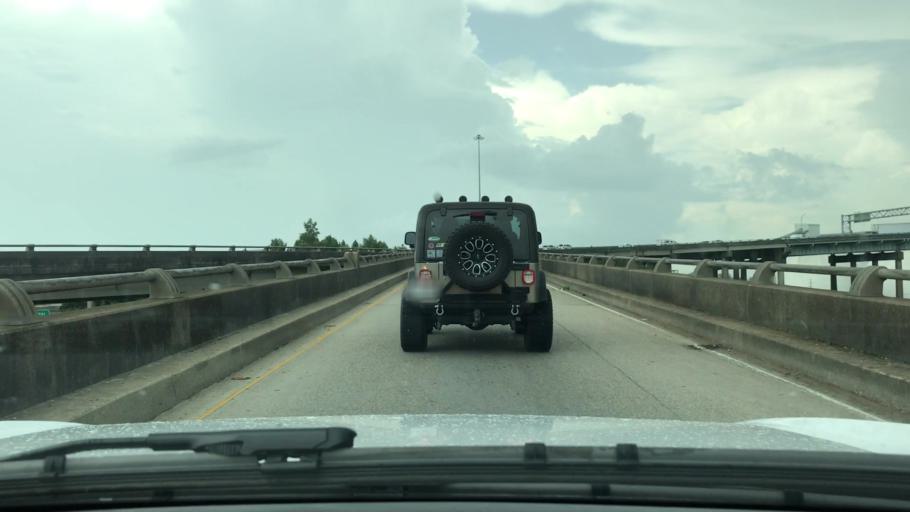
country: US
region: Louisiana
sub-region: West Baton Rouge Parish
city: Port Allen
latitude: 30.4382
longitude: -91.2082
